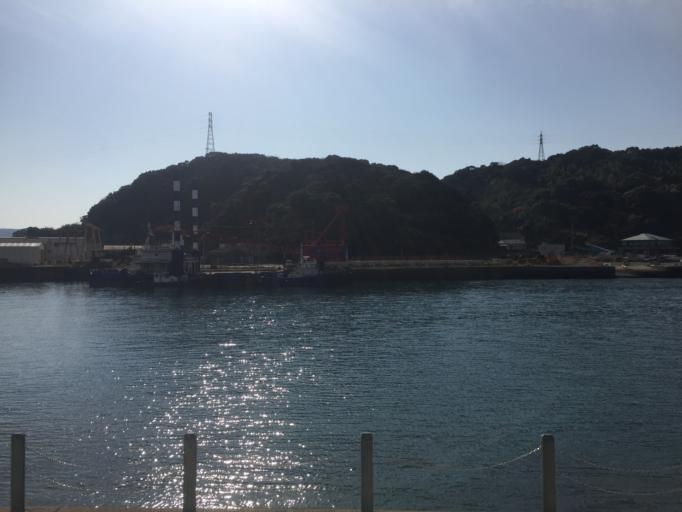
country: JP
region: Nagasaki
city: Nagasaki-shi
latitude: 32.6868
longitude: 129.8123
